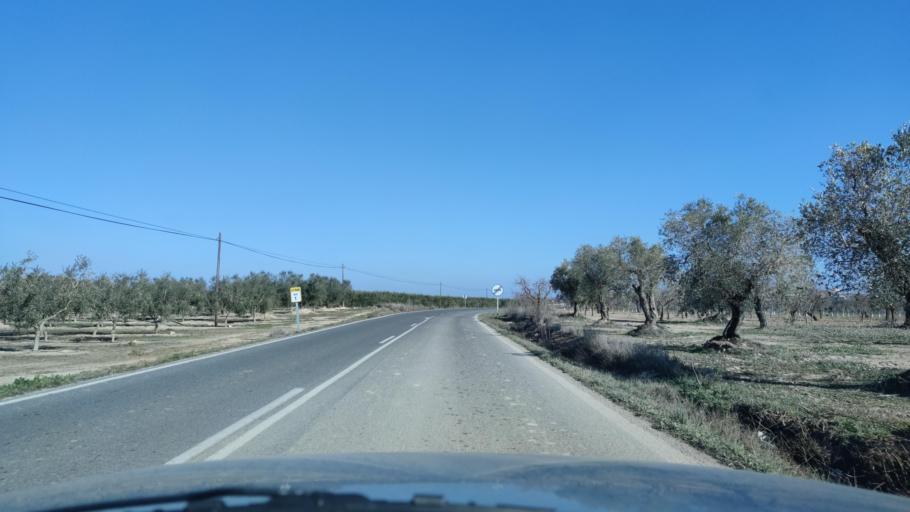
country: ES
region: Catalonia
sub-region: Provincia de Lleida
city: Maials
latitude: 41.3620
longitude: 0.4868
